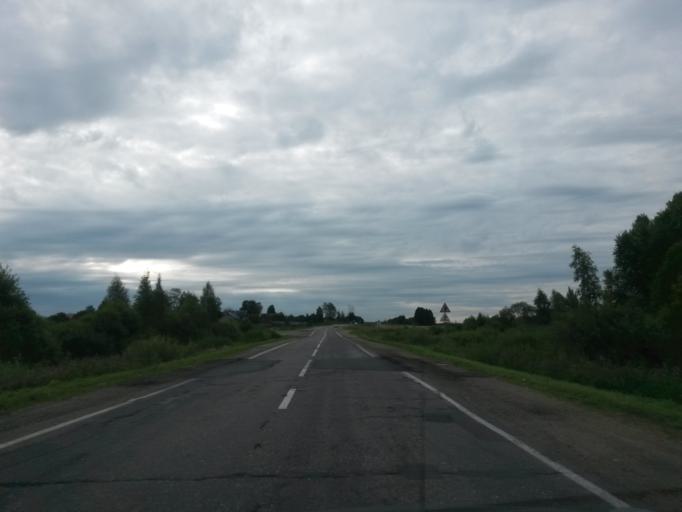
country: RU
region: Jaroslavl
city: Krasnyye Tkachi
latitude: 57.3976
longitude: 39.6704
